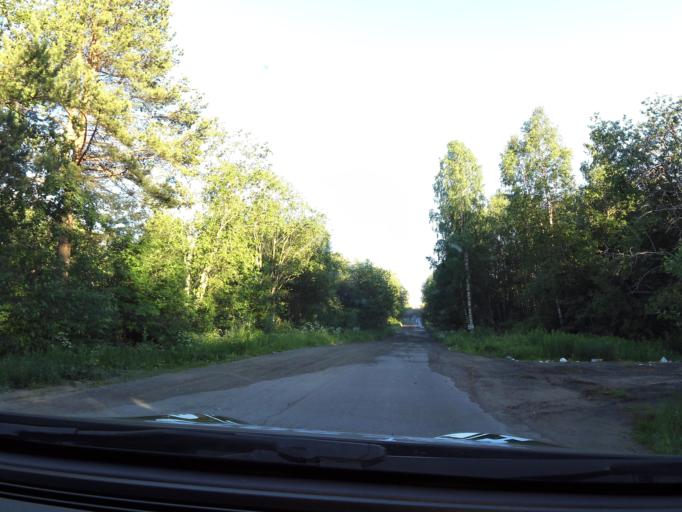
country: RU
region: Leningrad
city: Voznesen'ye
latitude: 61.1845
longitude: 35.5865
